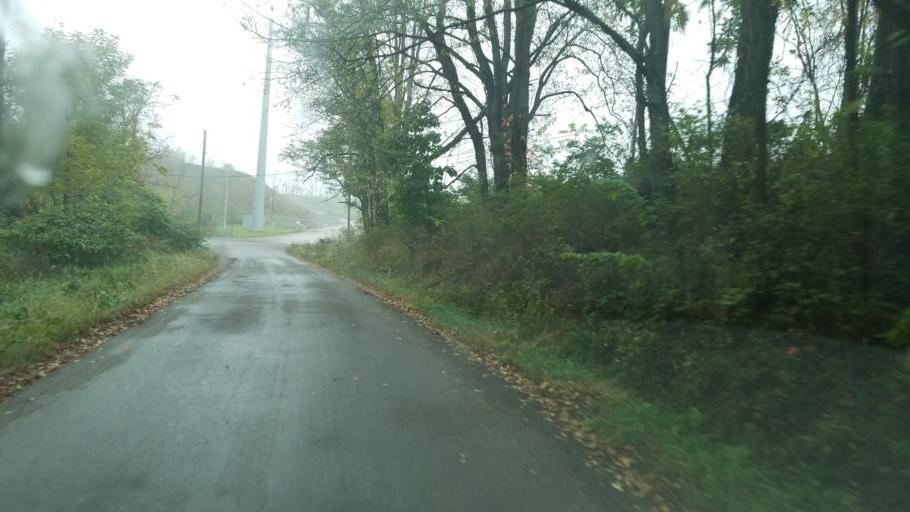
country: US
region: Ohio
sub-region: Harrison County
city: Cadiz
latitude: 40.3881
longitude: -81.1096
